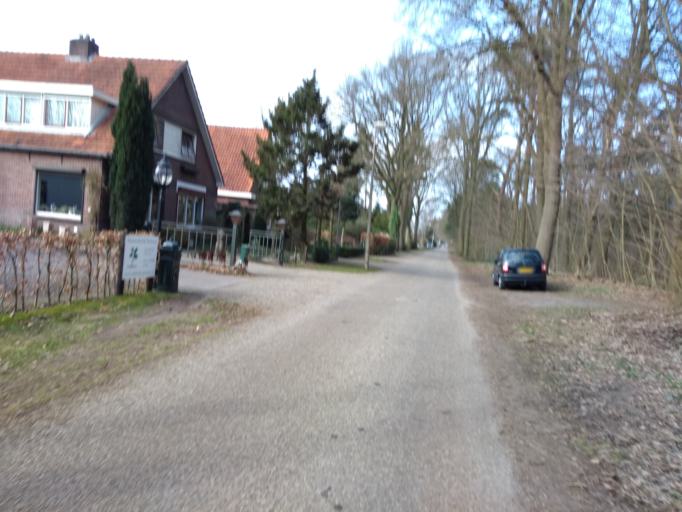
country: NL
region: Overijssel
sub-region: Gemeente Almelo
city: Almelo
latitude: 52.3329
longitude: 6.6673
